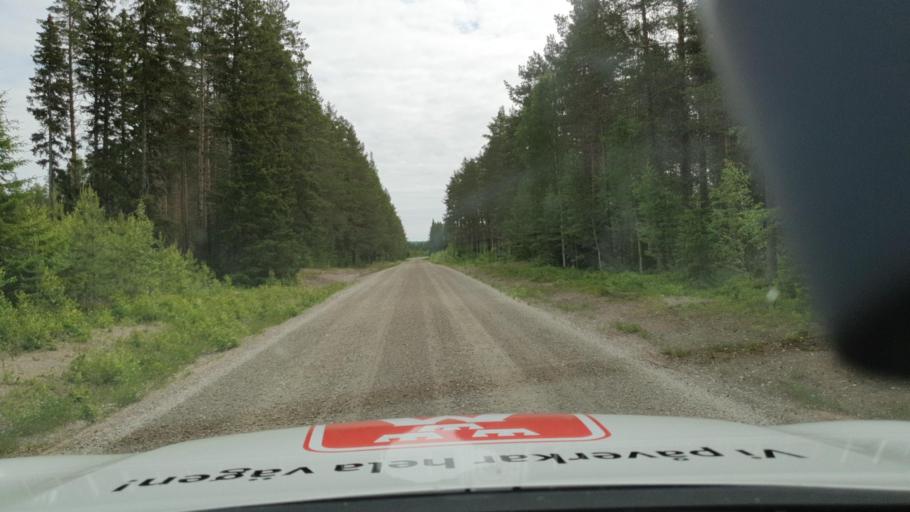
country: SE
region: Vaesterbotten
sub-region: Skelleftea Kommun
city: Forsbacka
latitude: 64.6554
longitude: 20.4269
